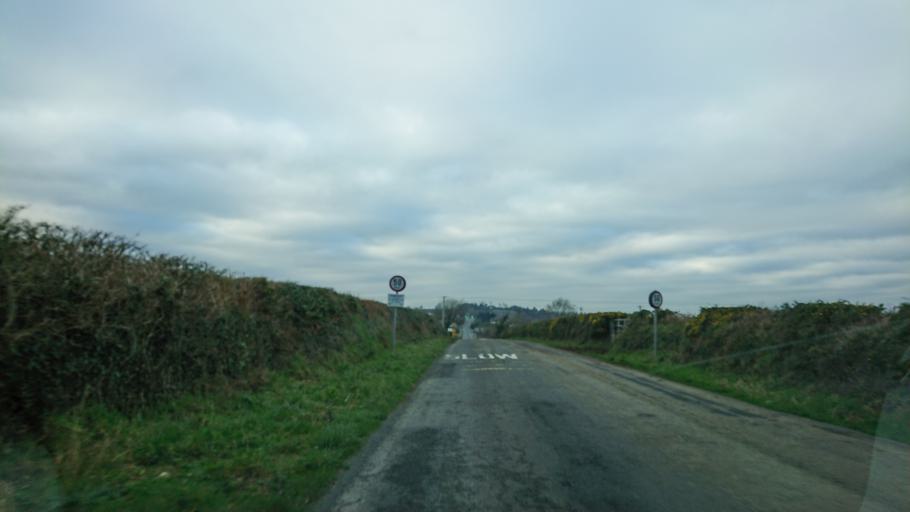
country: IE
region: Munster
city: Carrick-on-Suir
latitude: 52.3035
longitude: -7.4897
